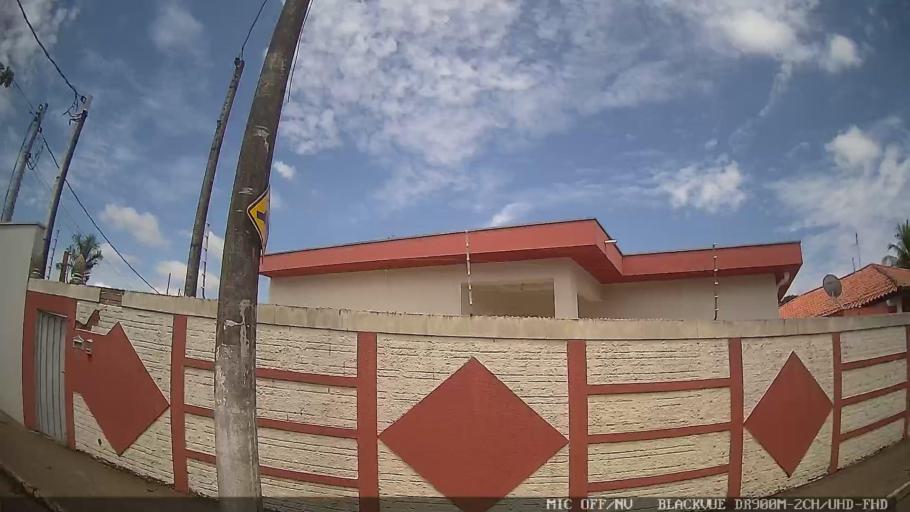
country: BR
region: Sao Paulo
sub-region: Laranjal Paulista
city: Laranjal Paulista
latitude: -23.0391
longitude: -47.8340
